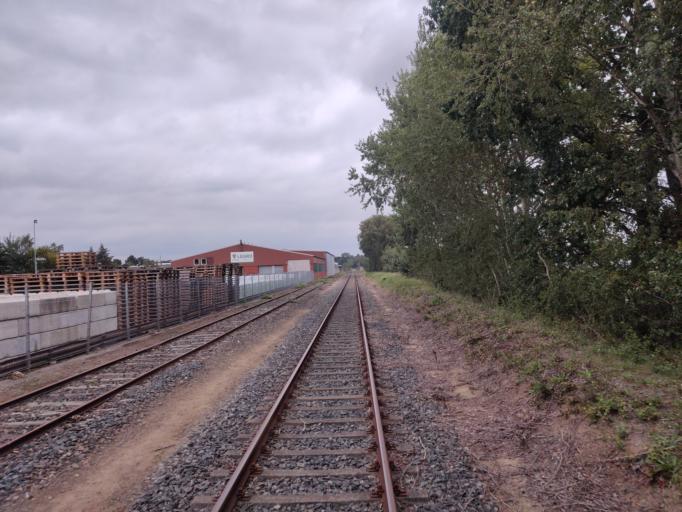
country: DE
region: Lower Saxony
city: Worpswede
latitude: 53.2570
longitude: 8.9591
